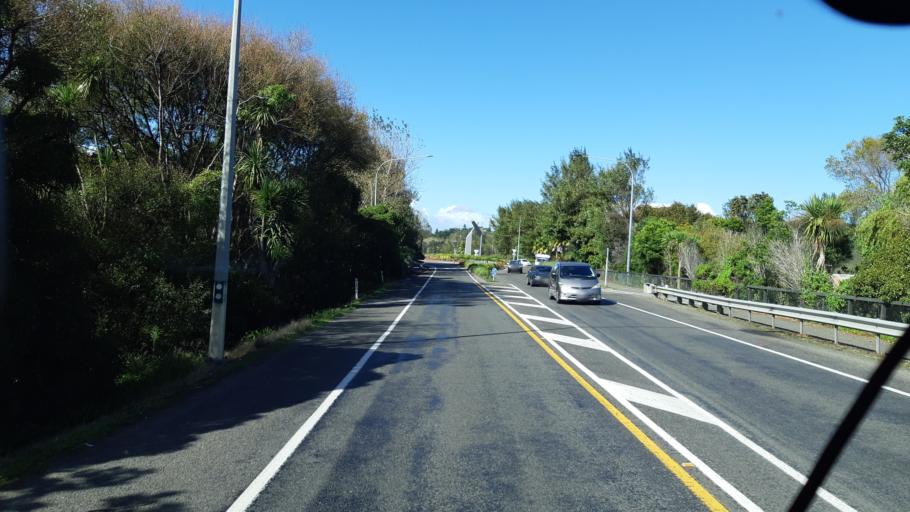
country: NZ
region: Manawatu-Wanganui
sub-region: Wanganui District
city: Wanganui
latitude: -39.9478
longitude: 175.0498
